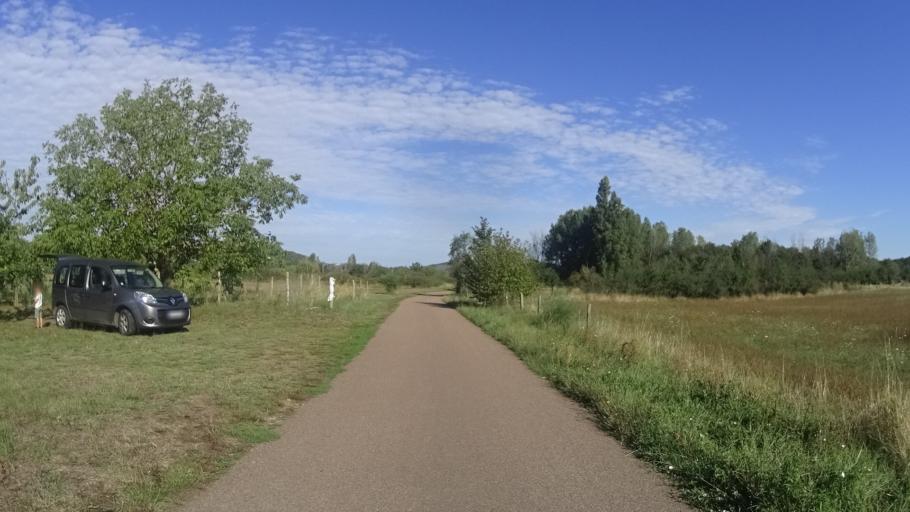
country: FR
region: Centre
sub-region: Departement du Cher
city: Sancerre
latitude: 47.3194
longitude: 2.8699
